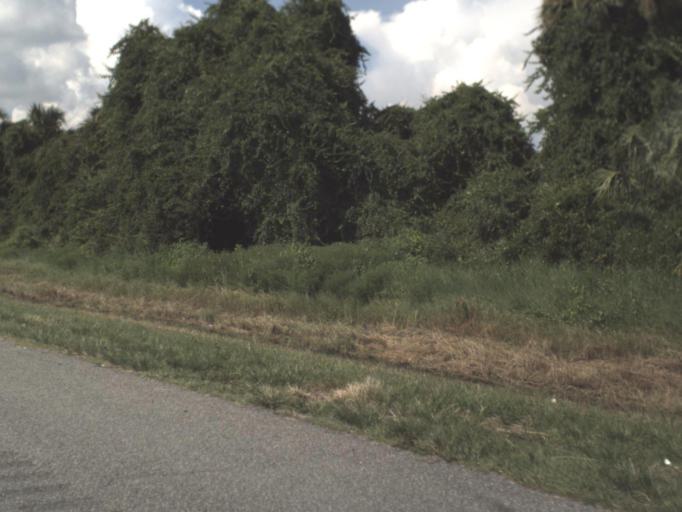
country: US
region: Florida
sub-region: Hillsborough County
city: Riverview
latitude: 27.8698
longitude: -82.3478
